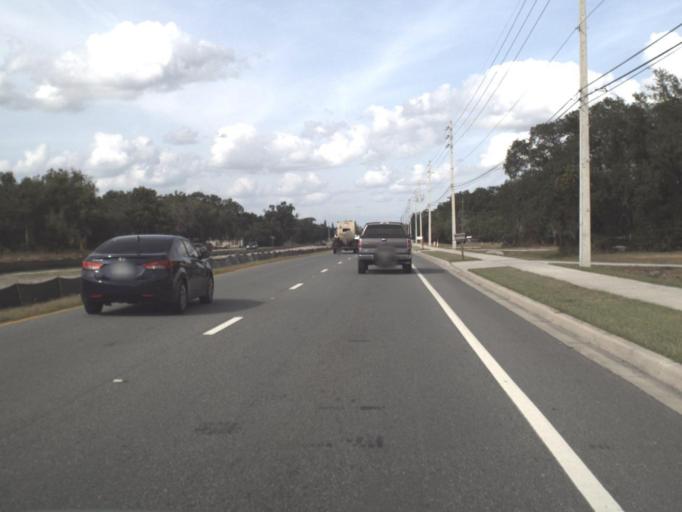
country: US
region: Florida
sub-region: Osceola County
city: Saint Cloud
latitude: 28.2845
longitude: -81.2438
